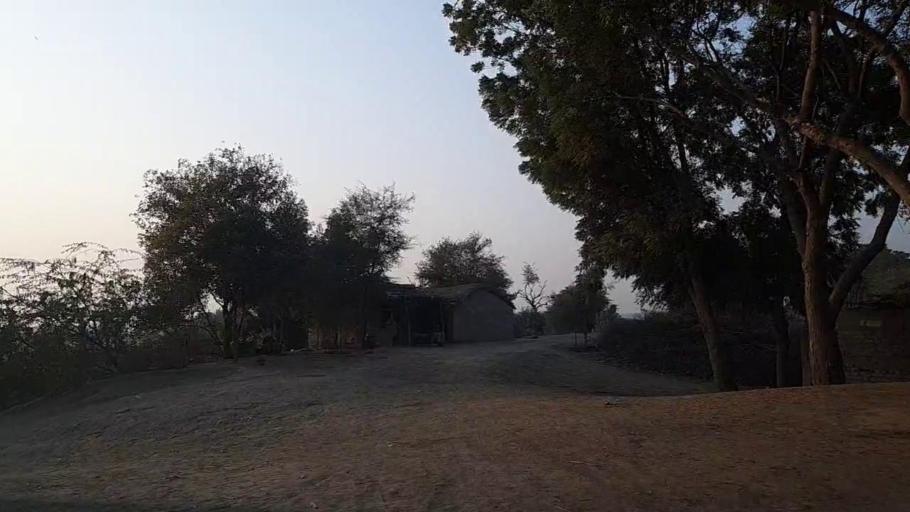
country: PK
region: Sindh
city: Sann
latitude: 26.1783
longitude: 68.0961
